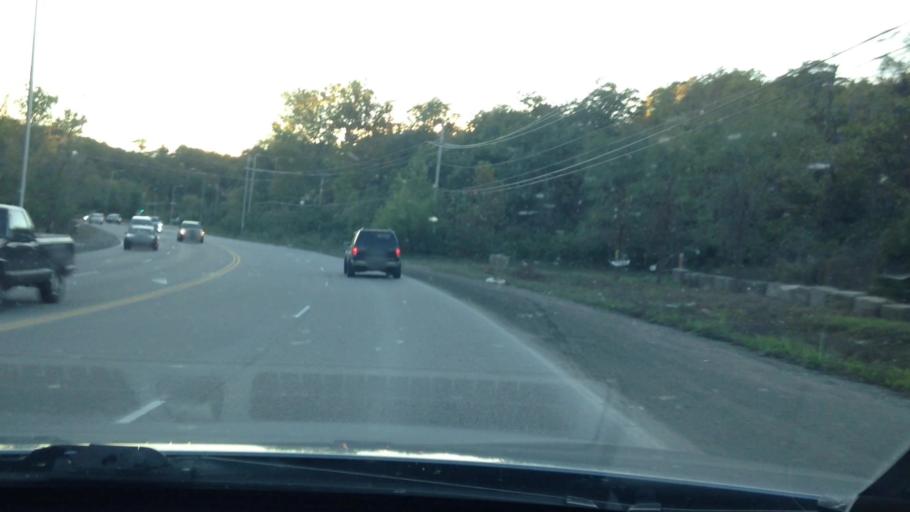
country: US
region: Missouri
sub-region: Jackson County
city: Raytown
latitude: 39.0136
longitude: -94.5032
